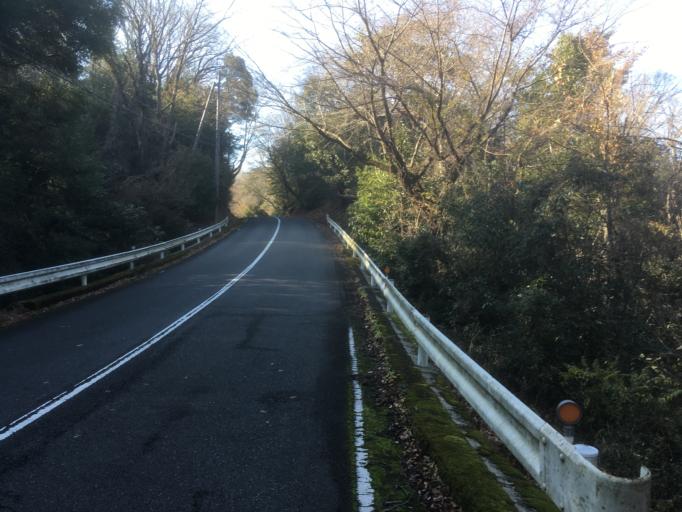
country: JP
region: Nara
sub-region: Ikoma-shi
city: Ikoma
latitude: 34.6939
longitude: 135.6775
